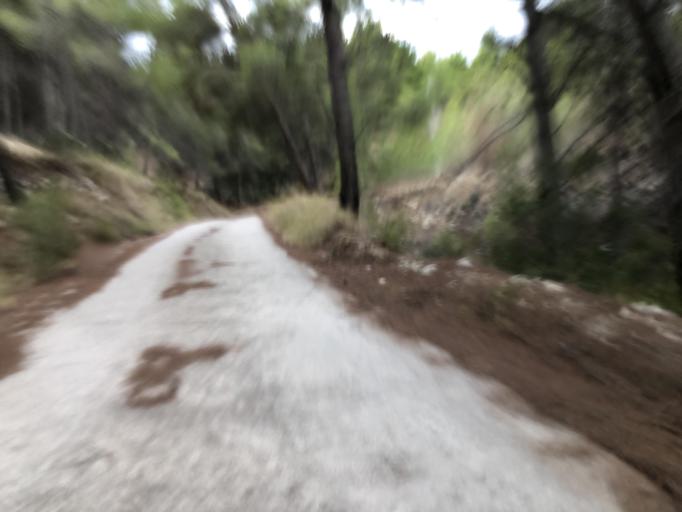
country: ES
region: Valencia
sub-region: Provincia de Alicante
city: Polop
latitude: 38.6392
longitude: -0.1364
